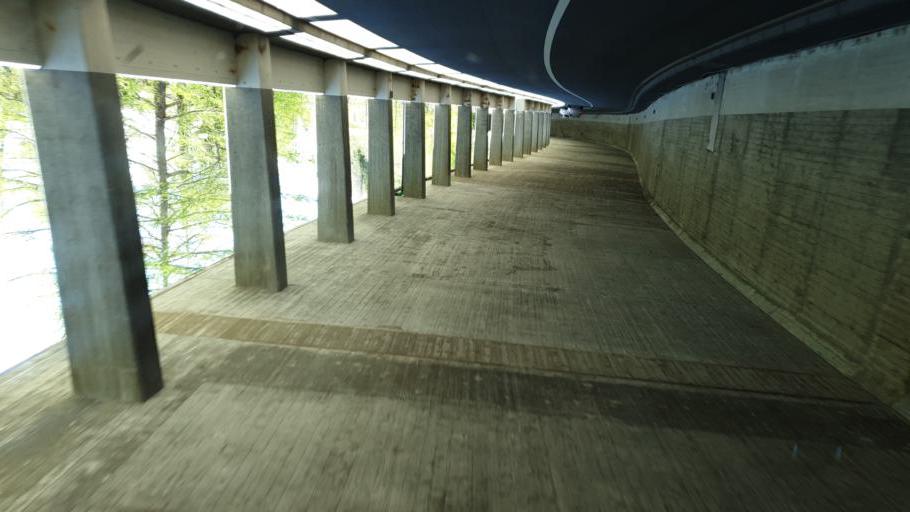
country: CH
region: Valais
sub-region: Brig District
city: Brig
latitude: 46.2723
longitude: 8.0398
